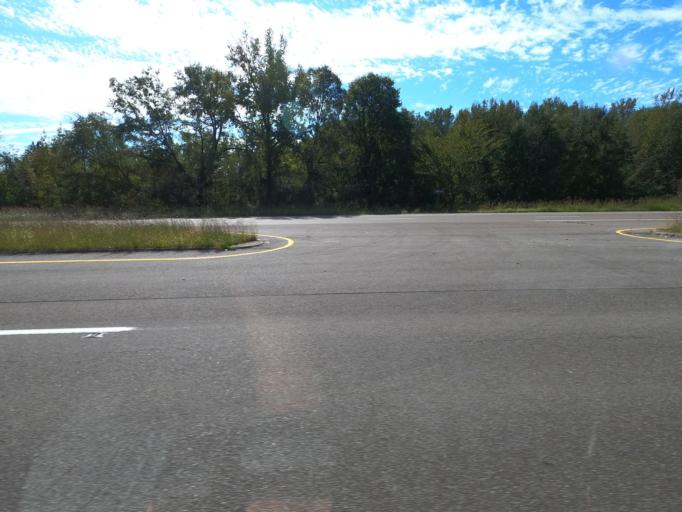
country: US
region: Tennessee
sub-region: Madison County
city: Three Way
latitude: 35.6706
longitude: -88.9378
